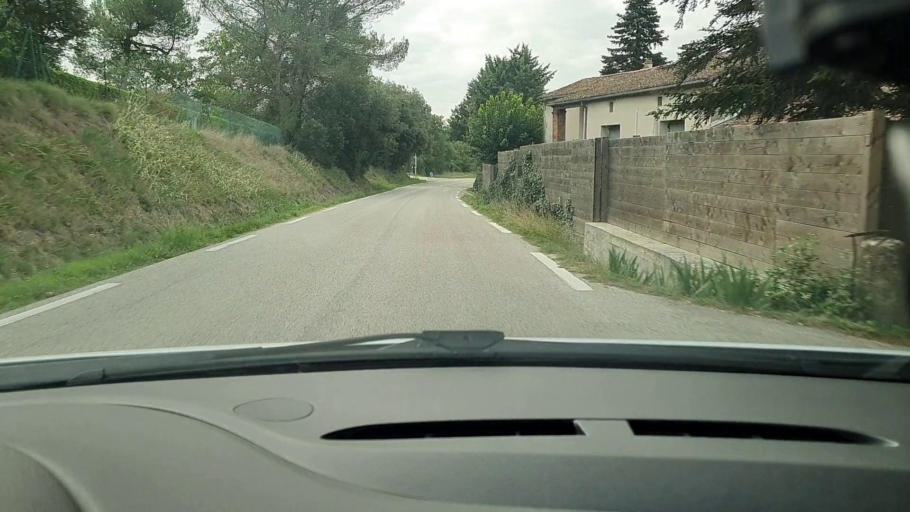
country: FR
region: Languedoc-Roussillon
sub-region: Departement du Gard
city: Mons
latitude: 44.1071
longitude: 4.2262
